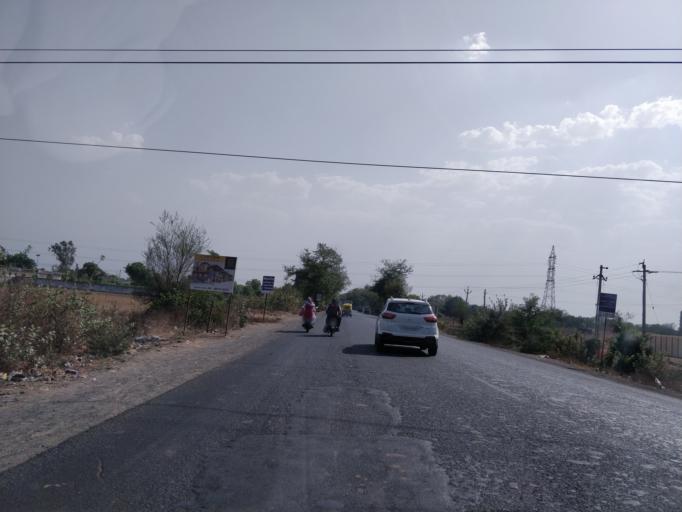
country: IN
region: Gujarat
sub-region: Ahmadabad
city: Naroda
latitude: 23.0923
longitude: 72.6921
